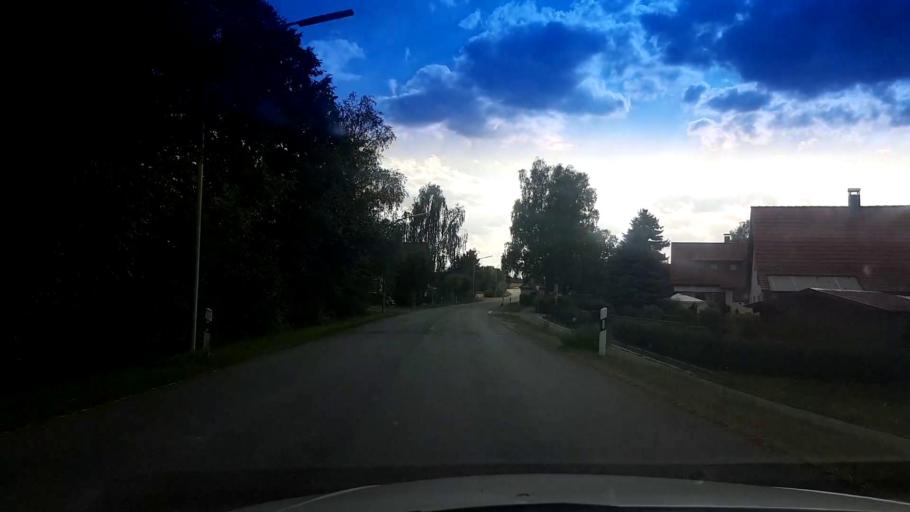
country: DE
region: Bavaria
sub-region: Upper Palatinate
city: Tirschenreuth
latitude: 49.9075
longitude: 12.3824
